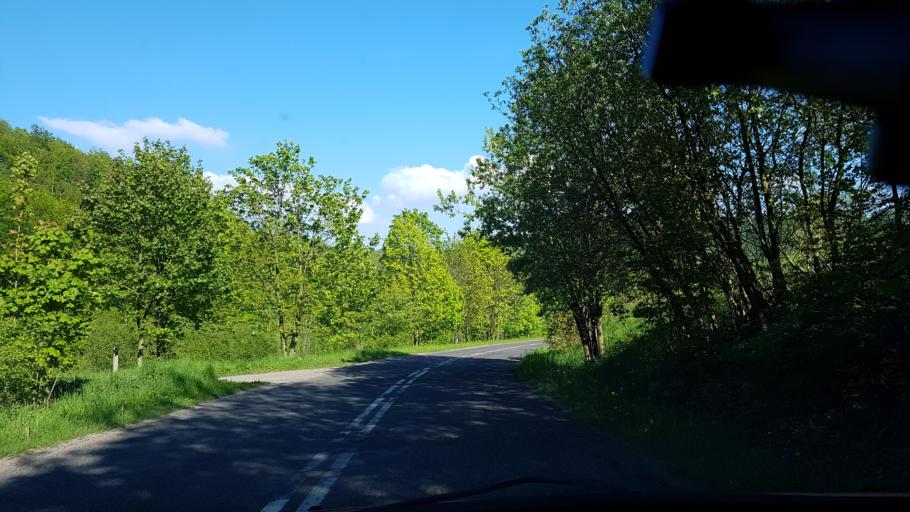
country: PL
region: Lower Silesian Voivodeship
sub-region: Powiat klodzki
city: Bozkow
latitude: 50.5732
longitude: 16.6069
